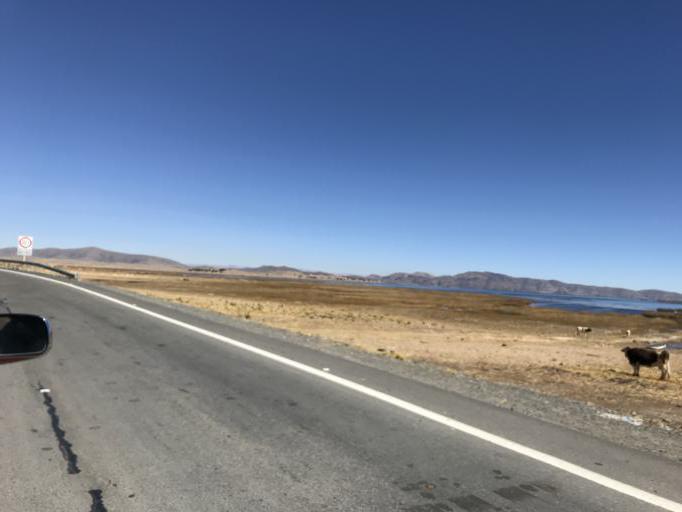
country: BO
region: La Paz
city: Huarina
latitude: -16.2381
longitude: -68.5767
